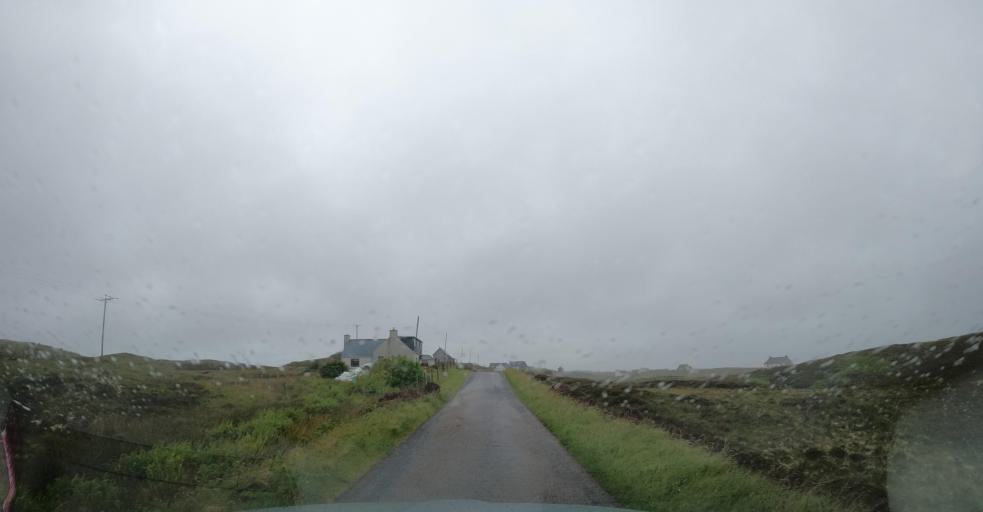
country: GB
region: Scotland
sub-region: Eilean Siar
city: Benbecula
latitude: 57.4857
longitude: -7.2169
